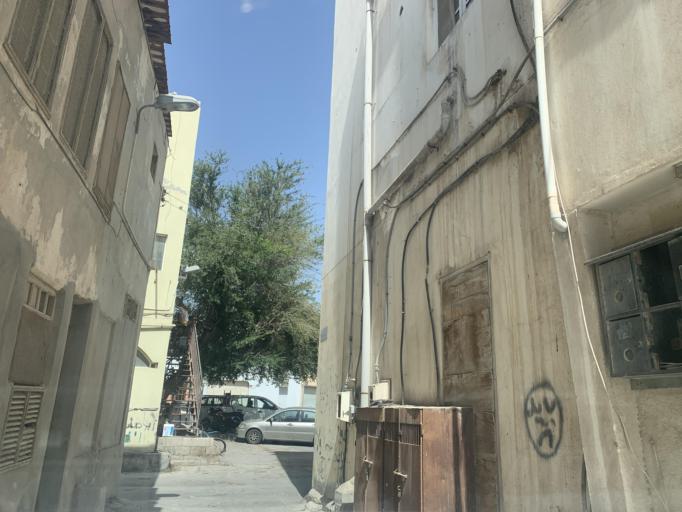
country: BH
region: Manama
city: Jidd Hafs
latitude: 26.2063
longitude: 50.5555
